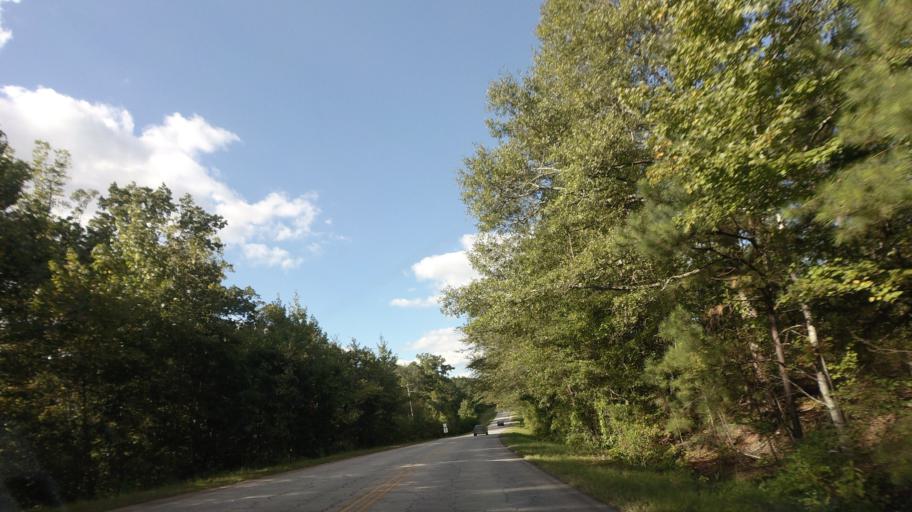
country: US
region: Georgia
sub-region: Lamar County
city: Barnesville
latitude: 33.0718
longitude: -84.1564
